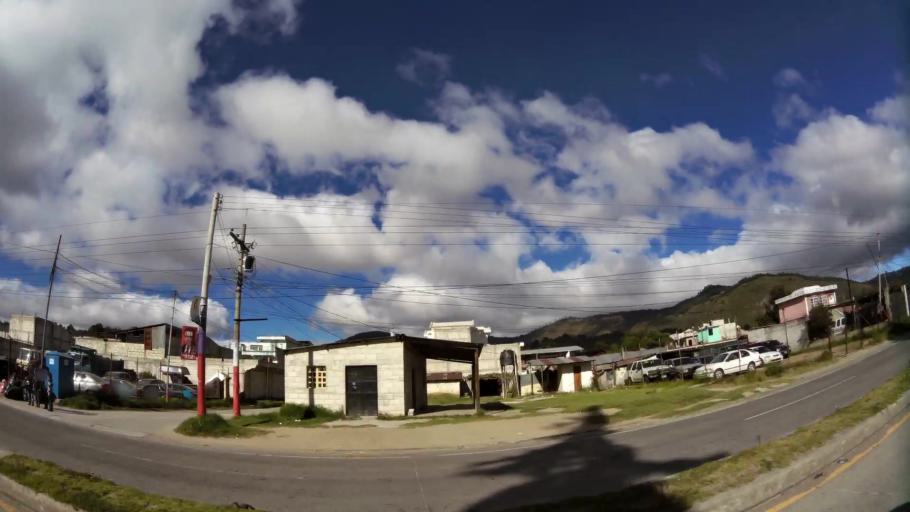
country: GT
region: Quetzaltenango
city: Salcaja
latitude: 14.8968
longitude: -91.4538
